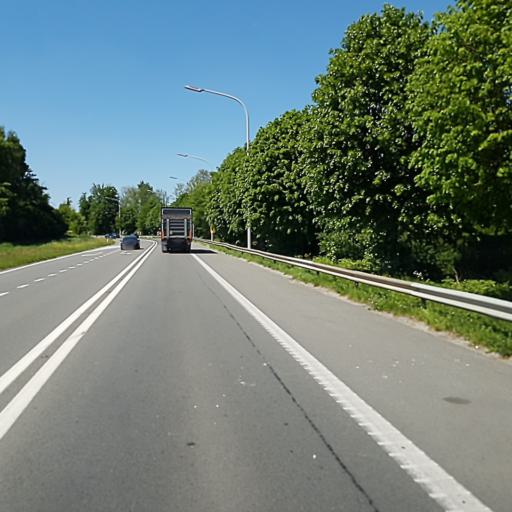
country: BE
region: Flanders
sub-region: Provincie Oost-Vlaanderen
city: Lede
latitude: 50.9288
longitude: 3.9579
